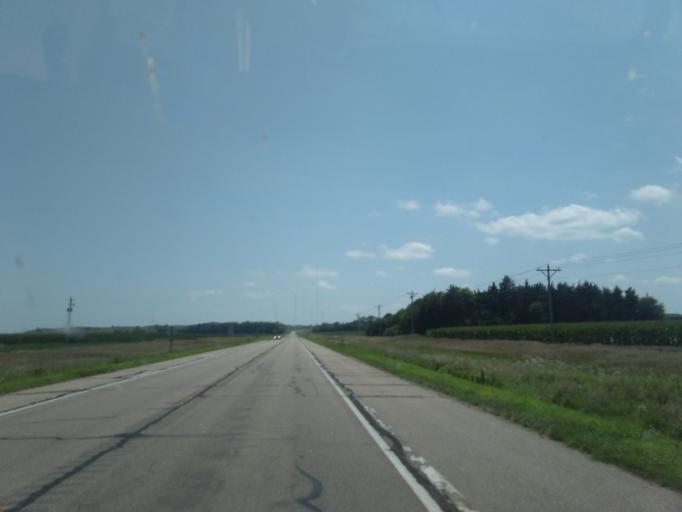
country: US
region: Nebraska
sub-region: Dawson County
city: Lexington
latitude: 40.7231
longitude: -99.7874
